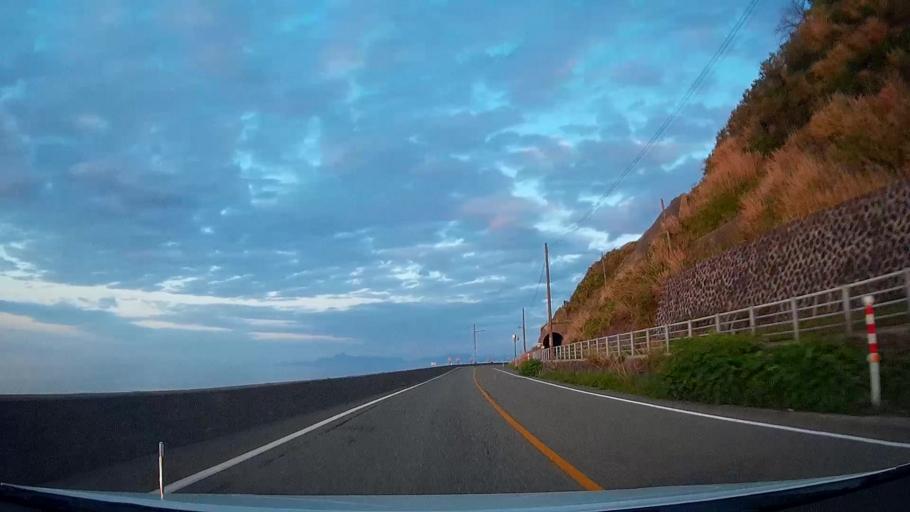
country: JP
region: Niigata
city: Joetsu
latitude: 37.1737
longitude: 138.0999
